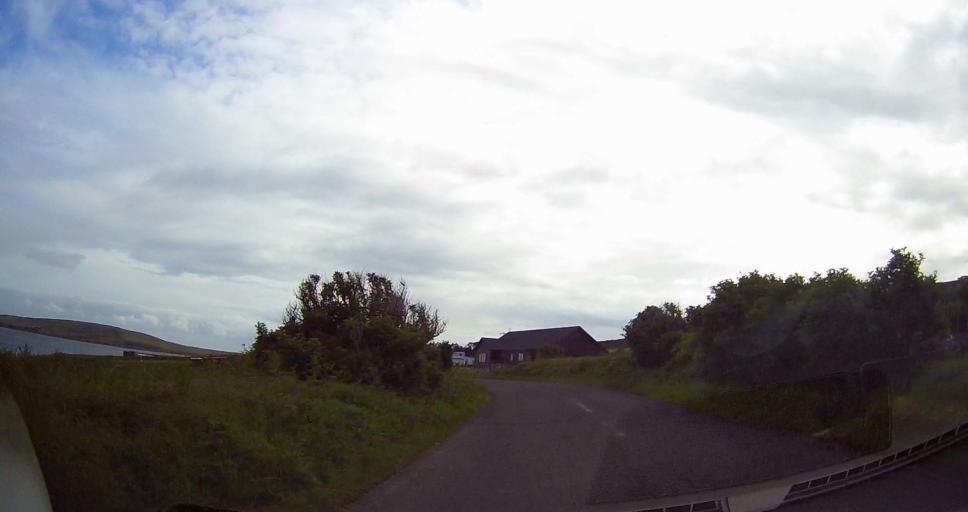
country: GB
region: Scotland
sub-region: Orkney Islands
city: Stromness
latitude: 58.7997
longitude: -3.2512
